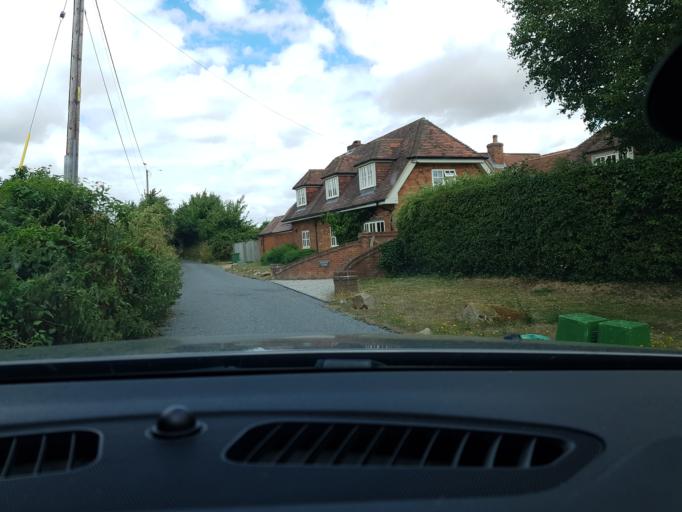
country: GB
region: England
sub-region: West Berkshire
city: Wickham
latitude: 51.4304
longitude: -1.4503
